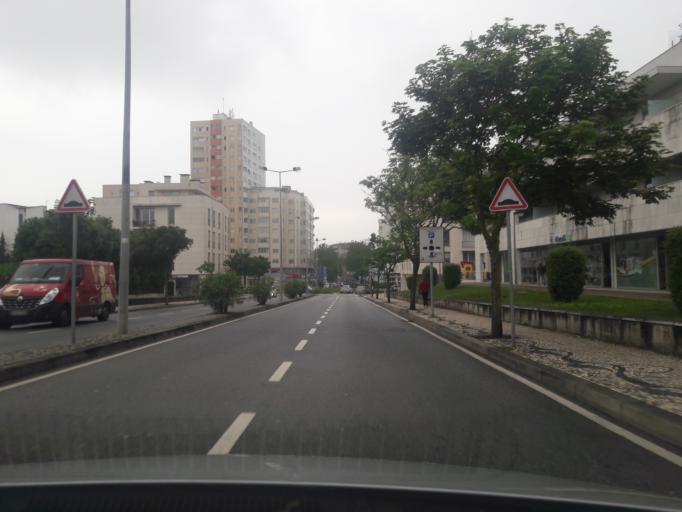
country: PT
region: Porto
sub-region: Povoa de Varzim
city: Povoa de Varzim
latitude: 41.3889
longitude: -8.7644
